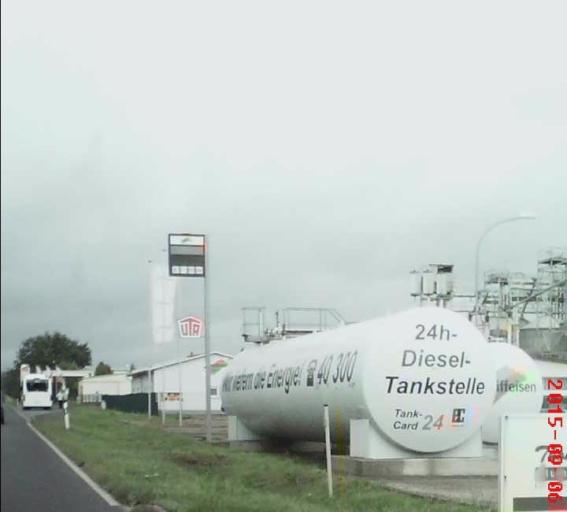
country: DE
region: Thuringia
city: Muehlhausen
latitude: 51.2247
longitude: 10.4540
